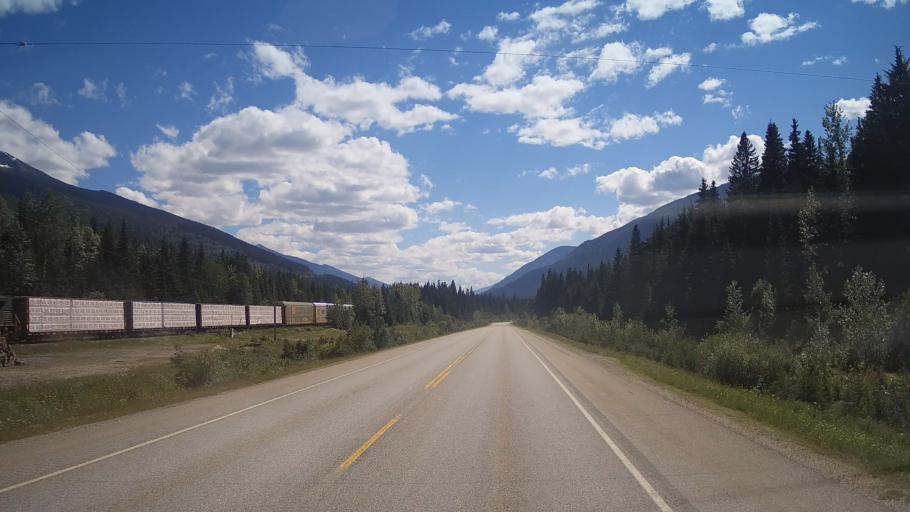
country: CA
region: Alberta
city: Jasper Park Lodge
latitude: 52.5756
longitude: -119.0982
